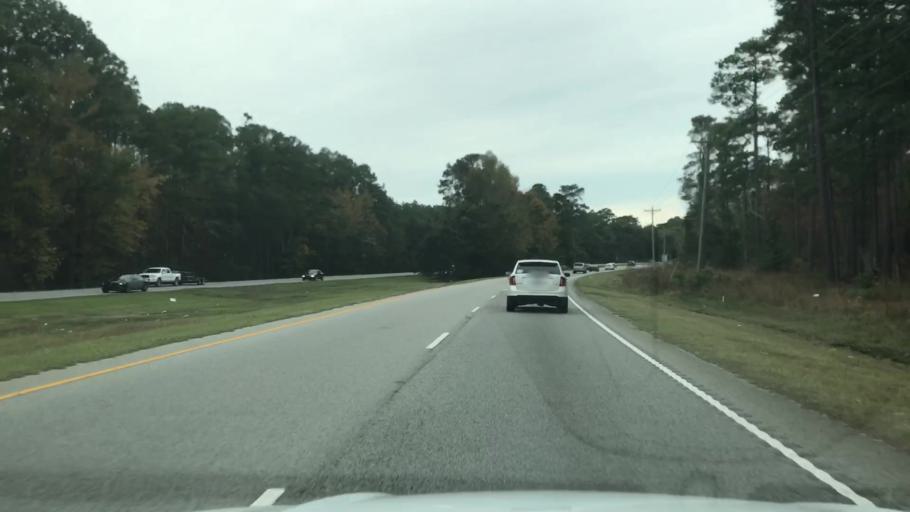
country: US
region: South Carolina
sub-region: Georgetown County
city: Georgetown
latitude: 33.3662
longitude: -79.2228
